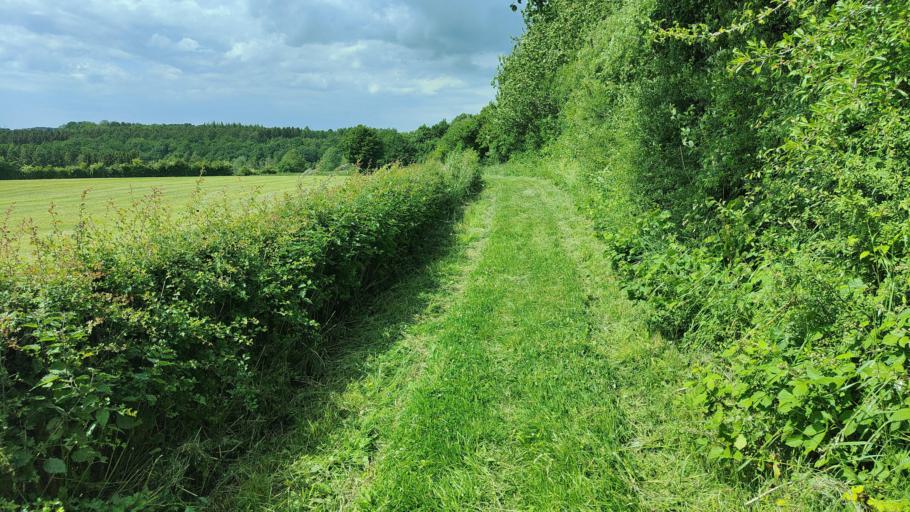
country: BE
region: Wallonia
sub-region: Province de Liege
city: La Calamine
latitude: 50.6997
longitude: 6.0481
